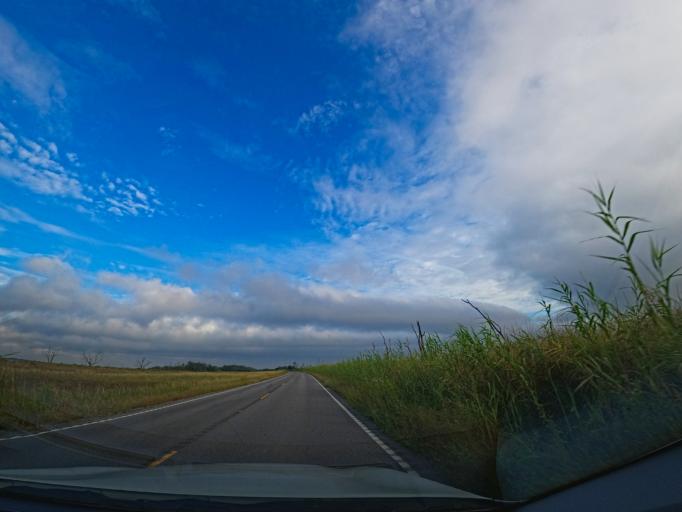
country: US
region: Louisiana
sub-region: Terrebonne Parish
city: Dulac
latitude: 29.3384
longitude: -90.6927
